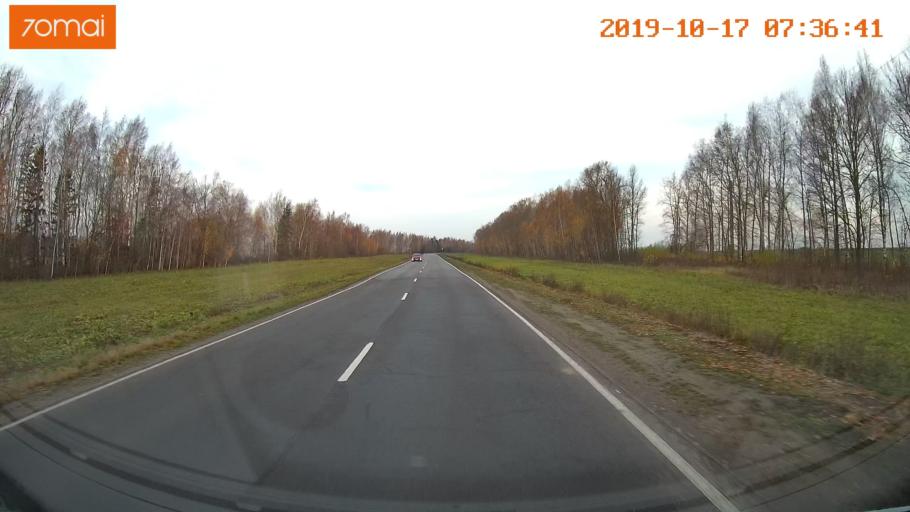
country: RU
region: Ivanovo
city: Gavrilov Posad
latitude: 56.4420
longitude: 39.9128
